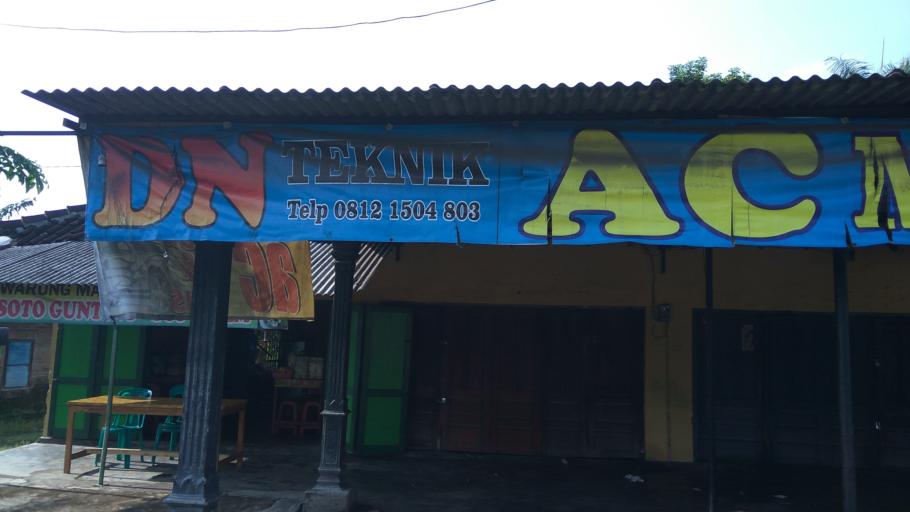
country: ID
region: Central Java
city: Ngemplak
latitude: -7.5351
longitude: 110.6781
